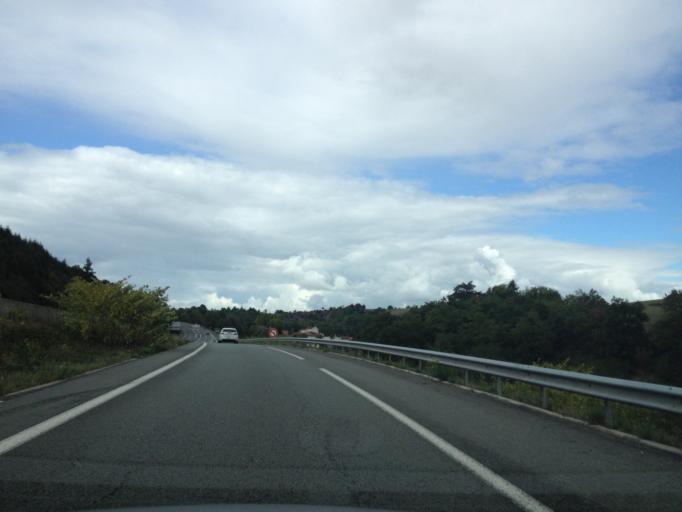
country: FR
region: Rhone-Alpes
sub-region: Departement de la Loire
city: Perreux
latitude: 45.9675
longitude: 4.1349
